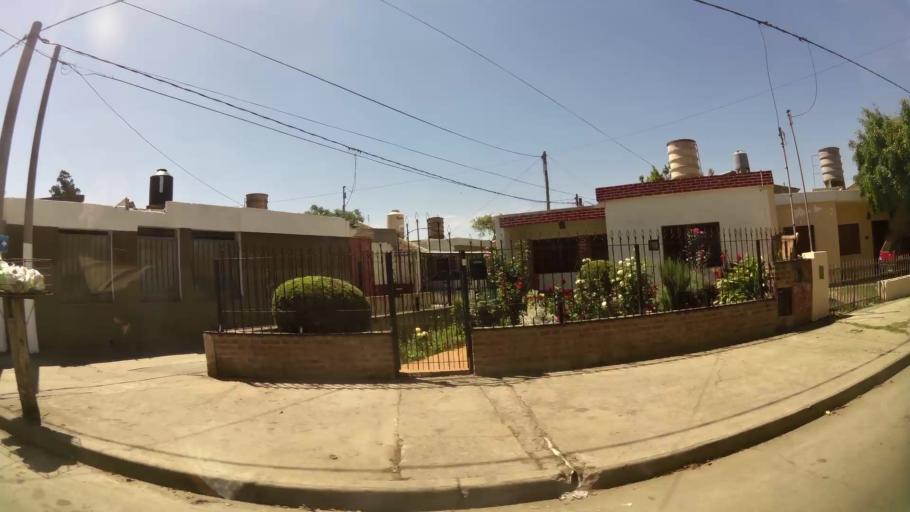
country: AR
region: Cordoba
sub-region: Departamento de Capital
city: Cordoba
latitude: -31.3828
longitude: -64.1525
